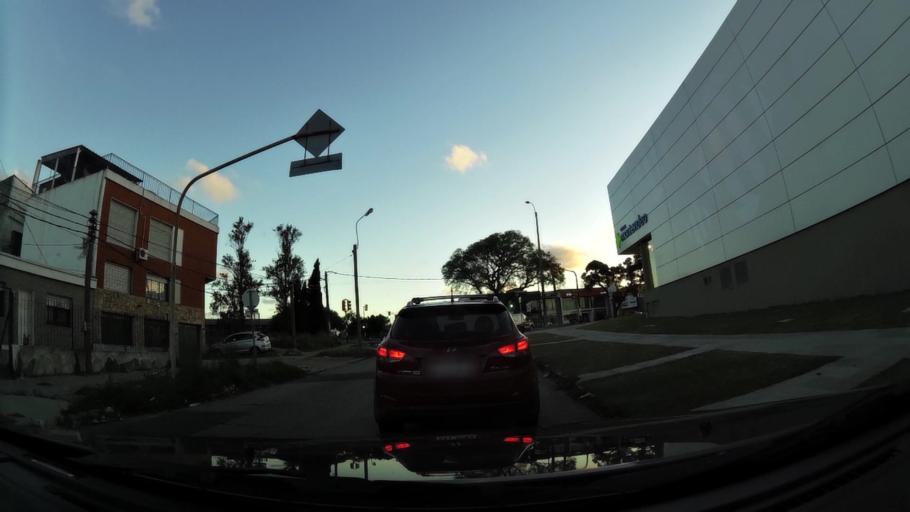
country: UY
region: Montevideo
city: Montevideo
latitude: -34.8866
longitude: -56.1212
